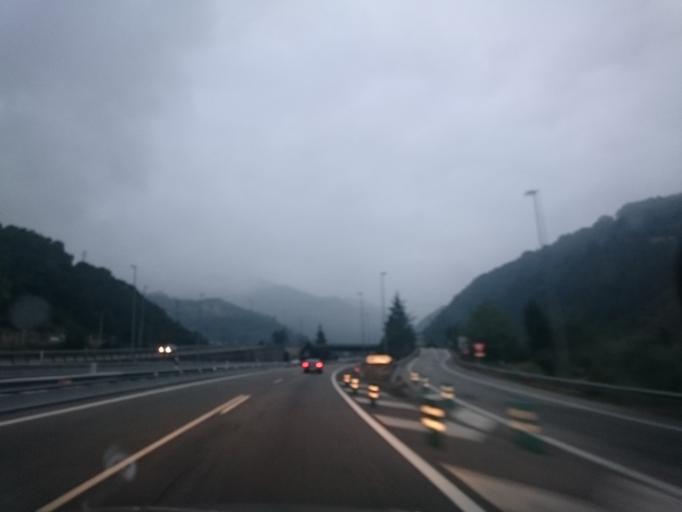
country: ES
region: Asturias
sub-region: Province of Asturias
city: Mieres
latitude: 43.2033
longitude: -5.7874
